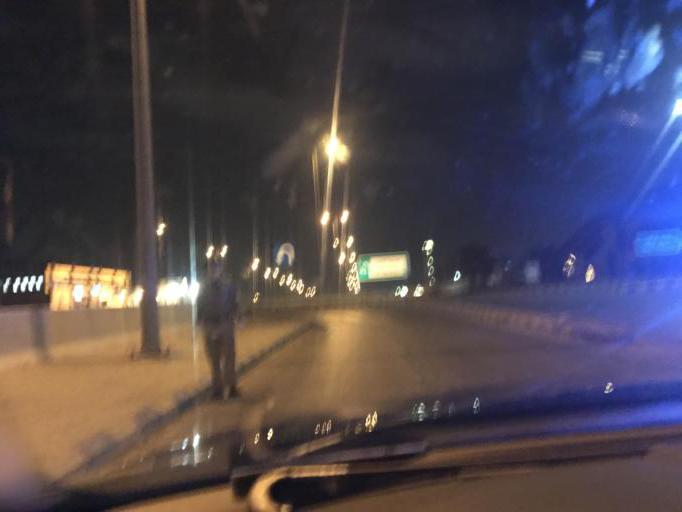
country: SA
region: Ar Riyad
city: Riyadh
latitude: 24.7808
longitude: 46.7063
